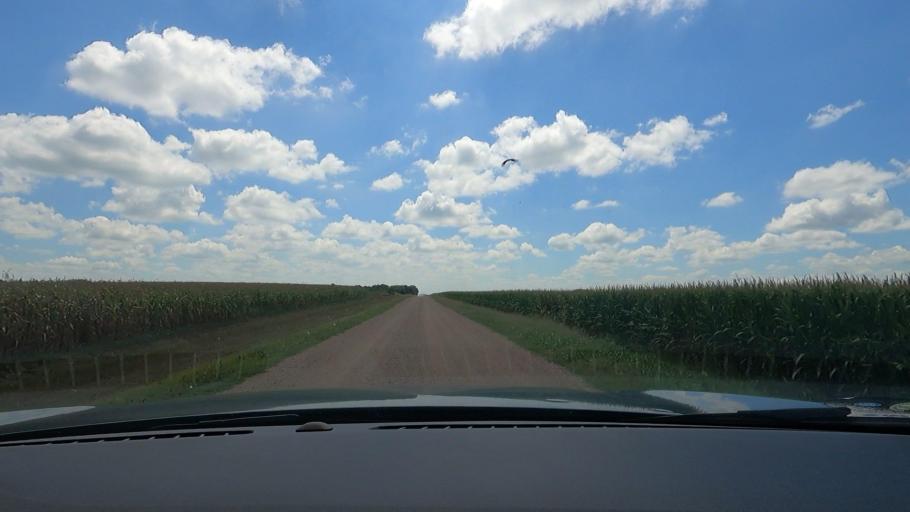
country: US
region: Nebraska
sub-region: Saunders County
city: Wahoo
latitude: 41.2720
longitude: -96.5418
